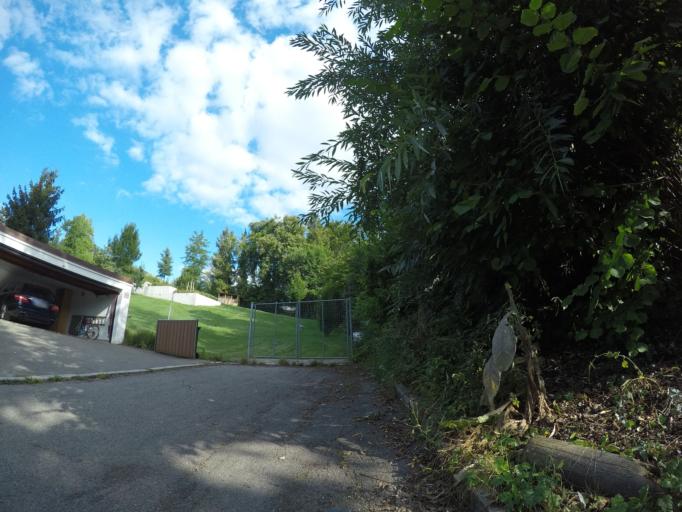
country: DE
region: Baden-Wuerttemberg
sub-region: Tuebingen Region
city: Reutlingen
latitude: 48.4762
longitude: 9.2098
